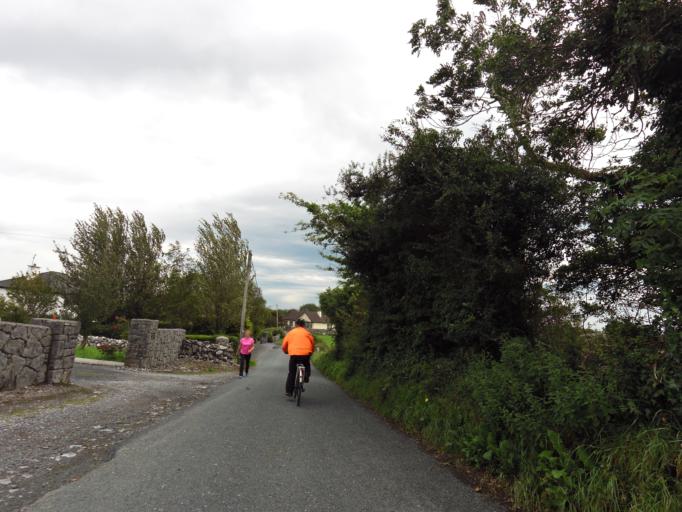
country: IE
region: Connaught
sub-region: County Galway
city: Gaillimh
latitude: 53.3150
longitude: -9.0410
